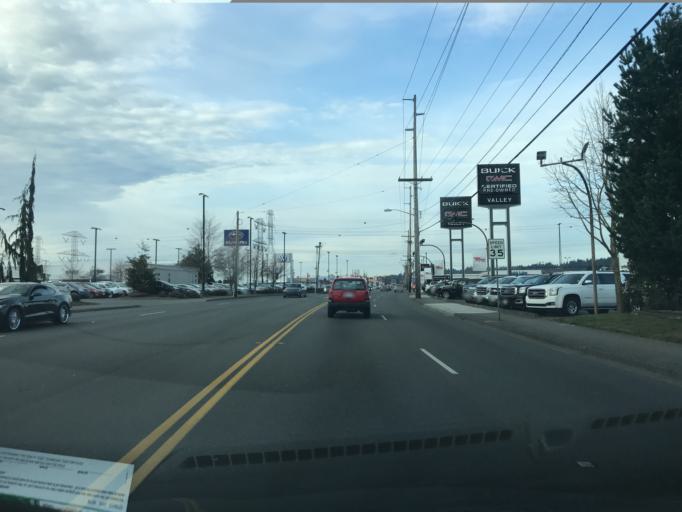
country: US
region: Washington
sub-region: King County
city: Auburn
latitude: 47.3342
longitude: -122.2221
